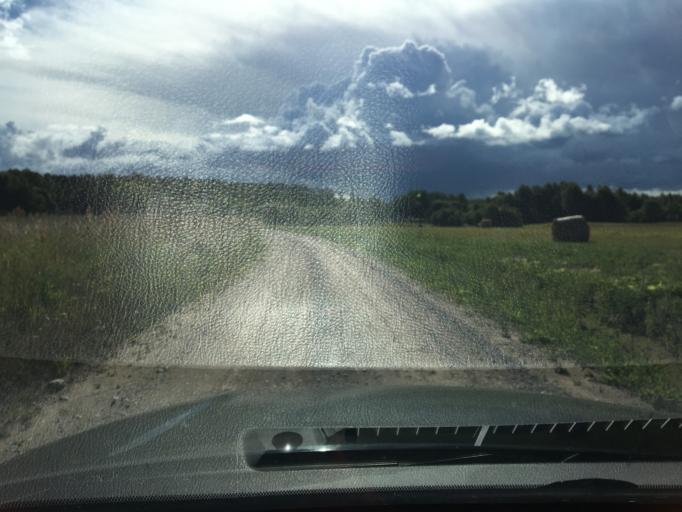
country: LV
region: Kuldigas Rajons
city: Kuldiga
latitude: 56.8421
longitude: 21.9558
